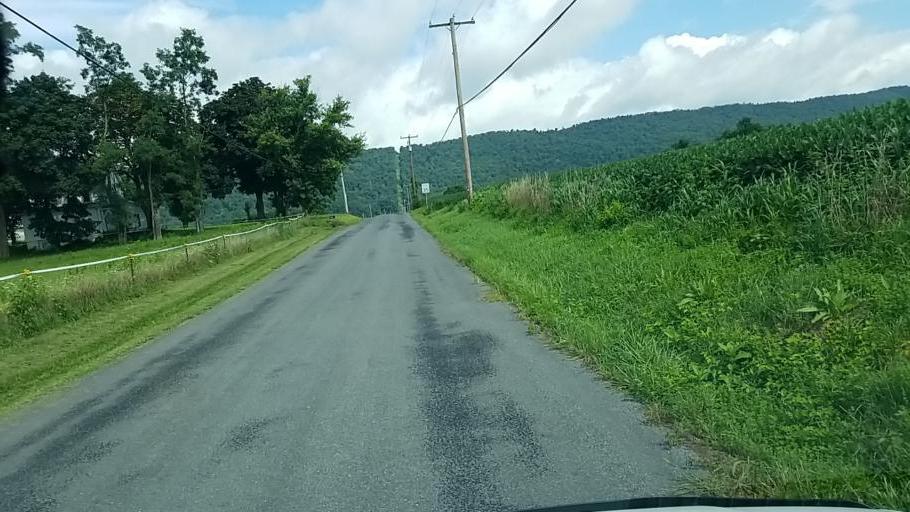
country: US
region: Pennsylvania
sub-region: Dauphin County
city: Millersburg
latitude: 40.5697
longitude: -76.9298
